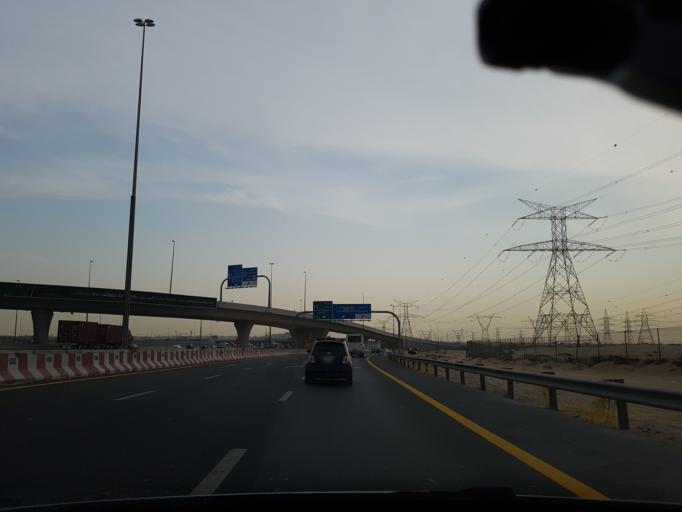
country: AE
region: Ash Shariqah
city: Sharjah
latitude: 25.2170
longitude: 55.4042
